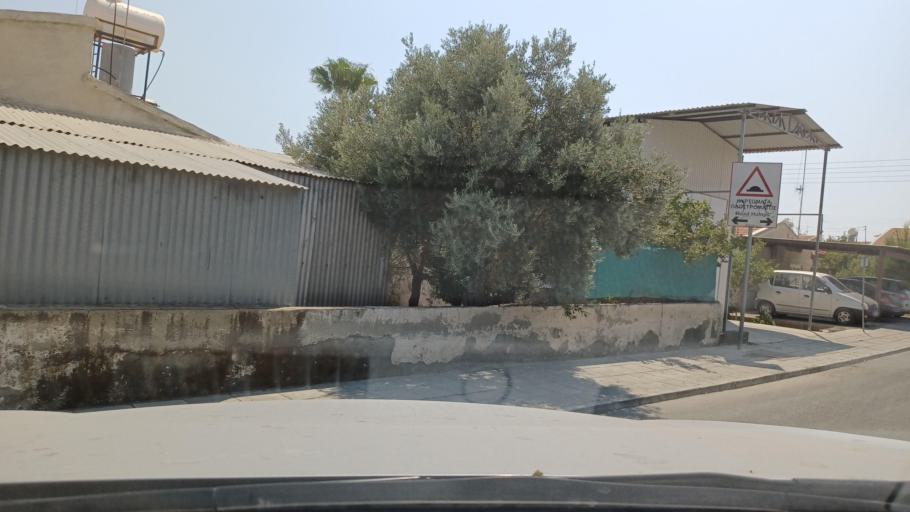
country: CY
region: Larnaka
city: Kolossi
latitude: 34.6791
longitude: 32.9430
